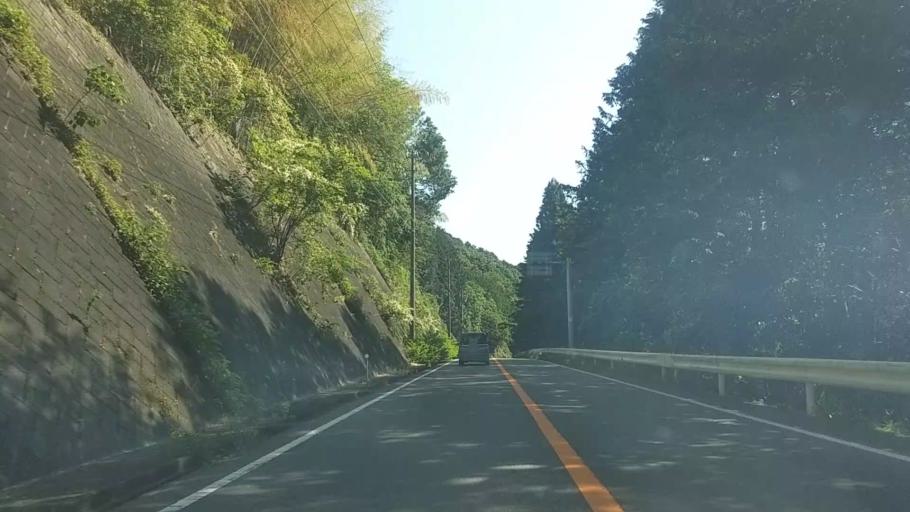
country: JP
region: Shizuoka
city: Fujinomiya
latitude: 35.1810
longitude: 138.5254
